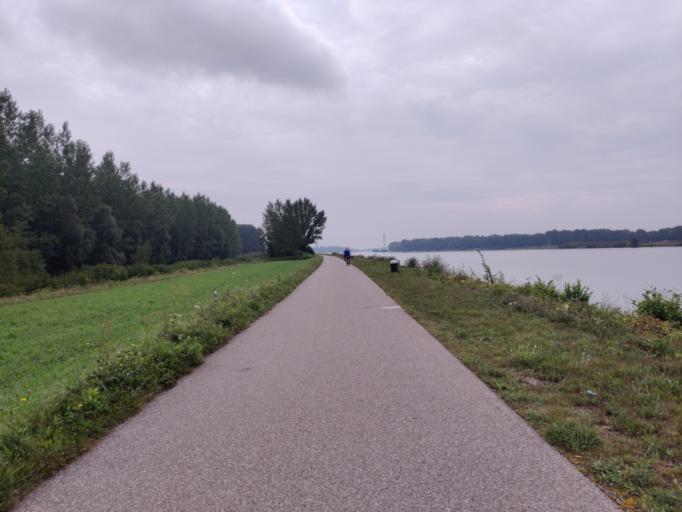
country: AT
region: Upper Austria
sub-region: Politischer Bezirk Urfahr-Umgebung
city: Steyregg
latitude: 48.2741
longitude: 14.3638
